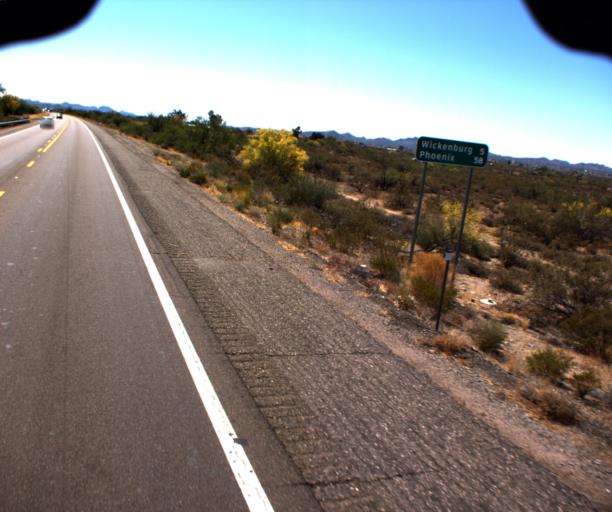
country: US
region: Arizona
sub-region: Maricopa County
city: Wickenburg
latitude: 34.0128
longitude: -112.7914
